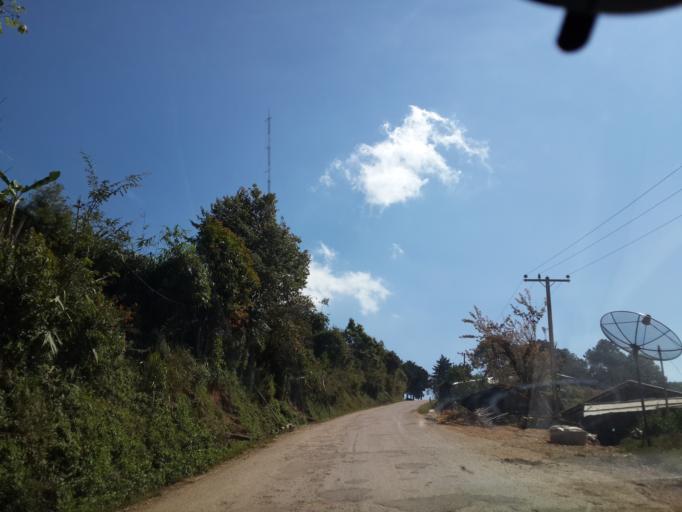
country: TH
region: Chiang Mai
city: Fang
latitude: 19.9358
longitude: 99.0417
